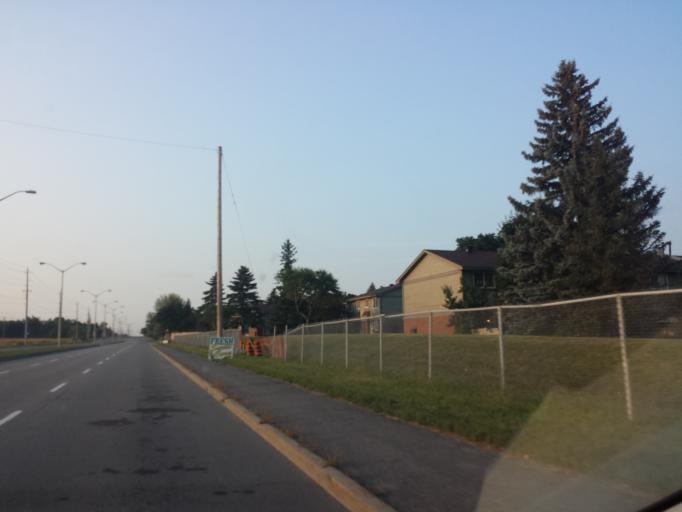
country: CA
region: Ontario
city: Bells Corners
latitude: 45.3088
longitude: -75.8795
